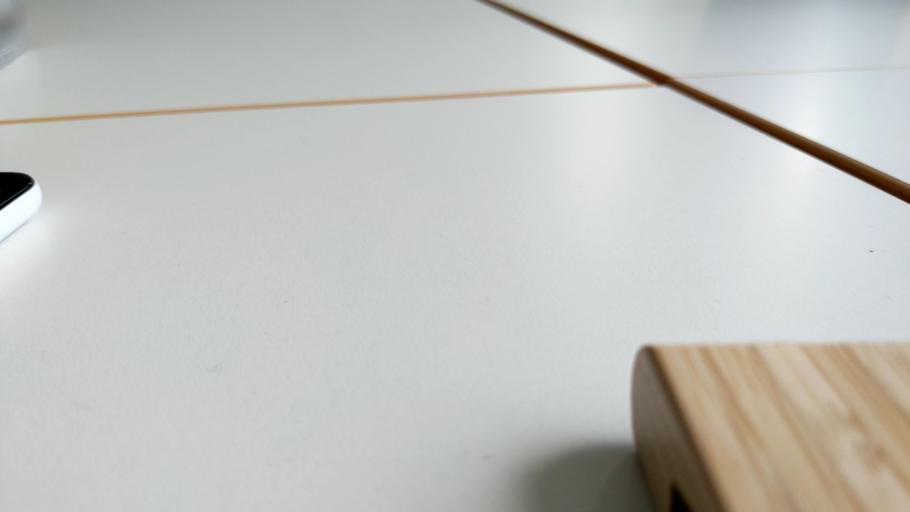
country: RU
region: Moscow
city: Yasenevo
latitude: 55.5767
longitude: 37.5194
